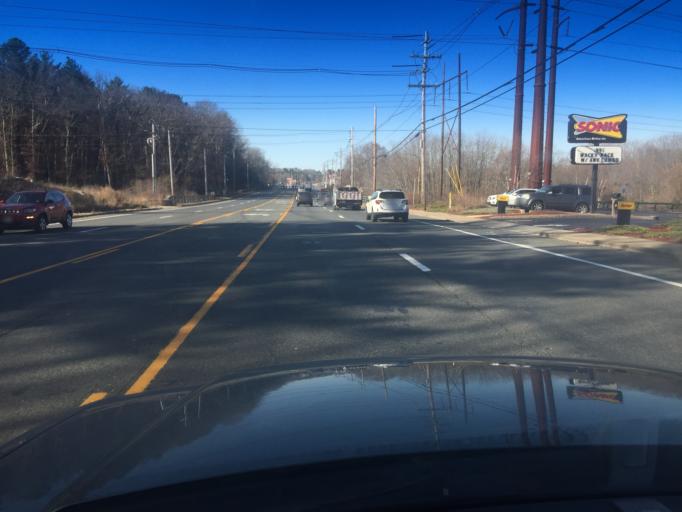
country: US
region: Rhode Island
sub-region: Providence County
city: Greenville
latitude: 41.8702
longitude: -71.5239
